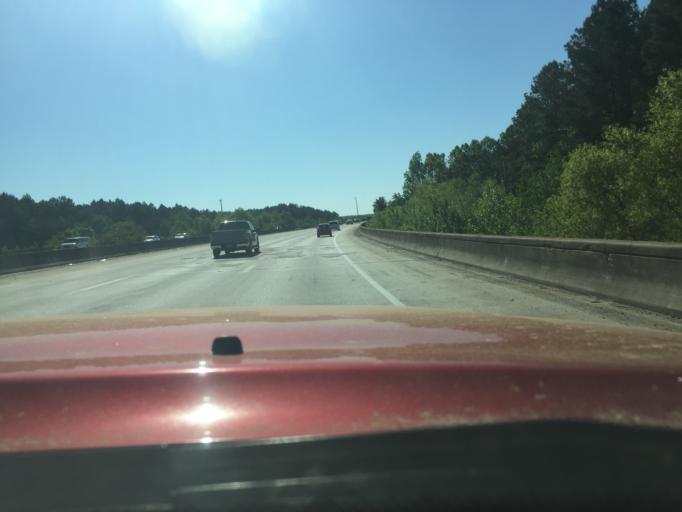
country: US
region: South Carolina
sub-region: Lexington County
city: Cayce
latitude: 33.9286
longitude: -81.0275
